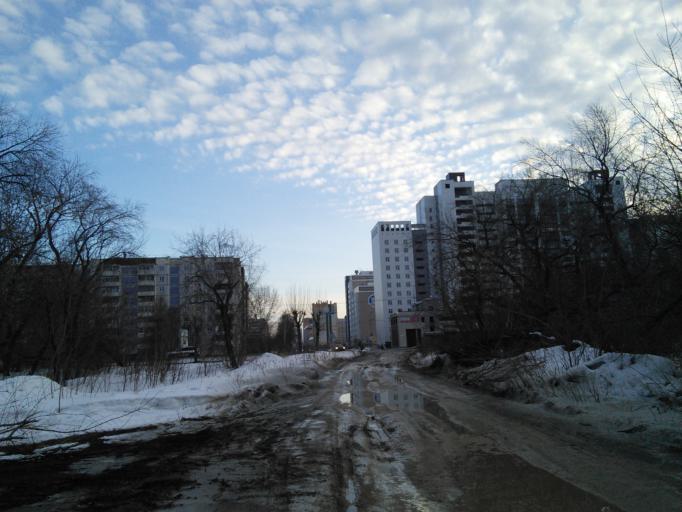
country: RU
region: Altai Krai
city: Novosilikatnyy
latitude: 53.3461
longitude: 83.6634
